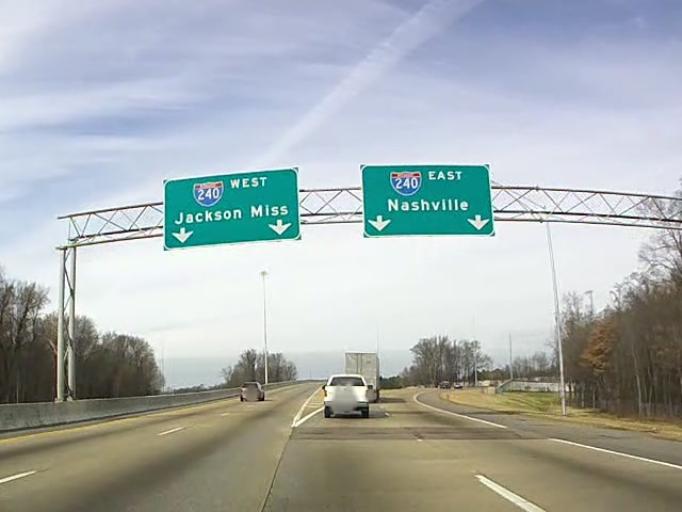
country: US
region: Tennessee
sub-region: Shelby County
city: Germantown
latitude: 35.0818
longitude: -89.8765
